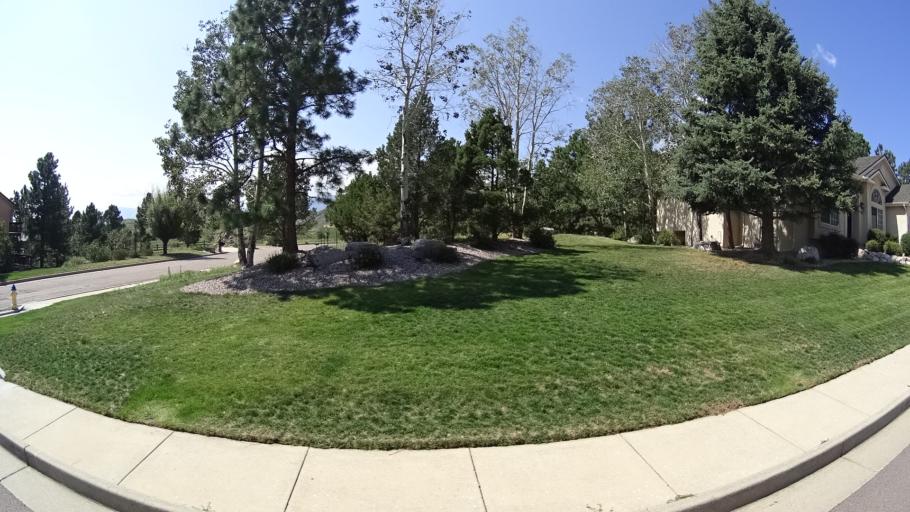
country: US
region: Colorado
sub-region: El Paso County
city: Manitou Springs
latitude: 38.9193
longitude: -104.8799
